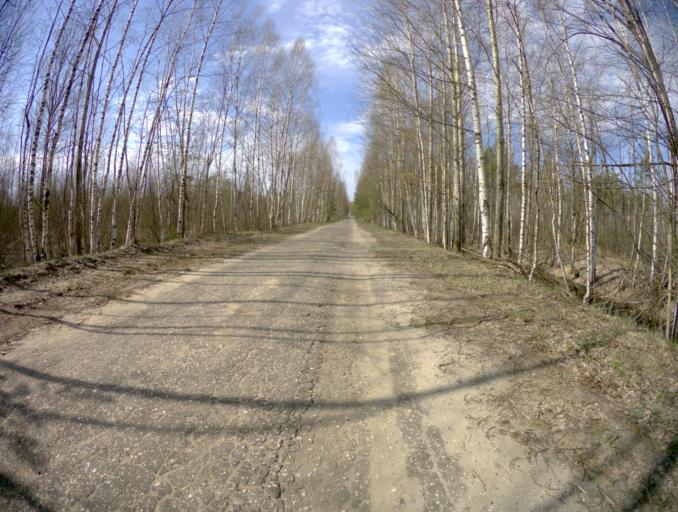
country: RU
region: Vladimir
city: Mezinovskiy
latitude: 55.5132
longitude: 40.3709
